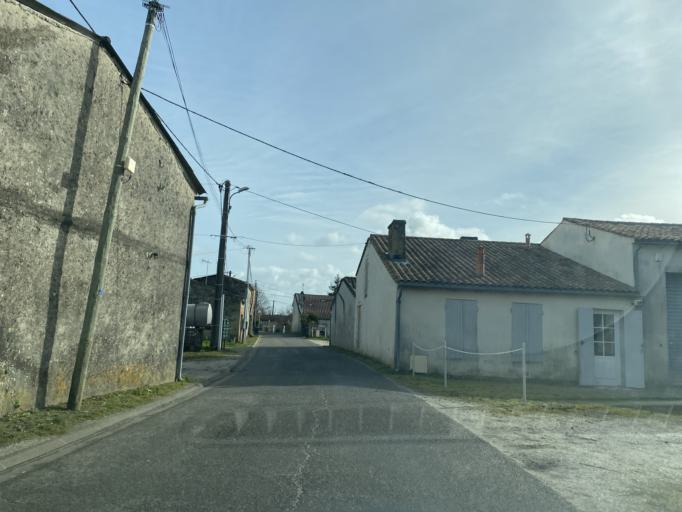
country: FR
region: Aquitaine
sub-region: Departement de la Gironde
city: Moulis-en-Medoc
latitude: 45.0556
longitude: -0.7690
